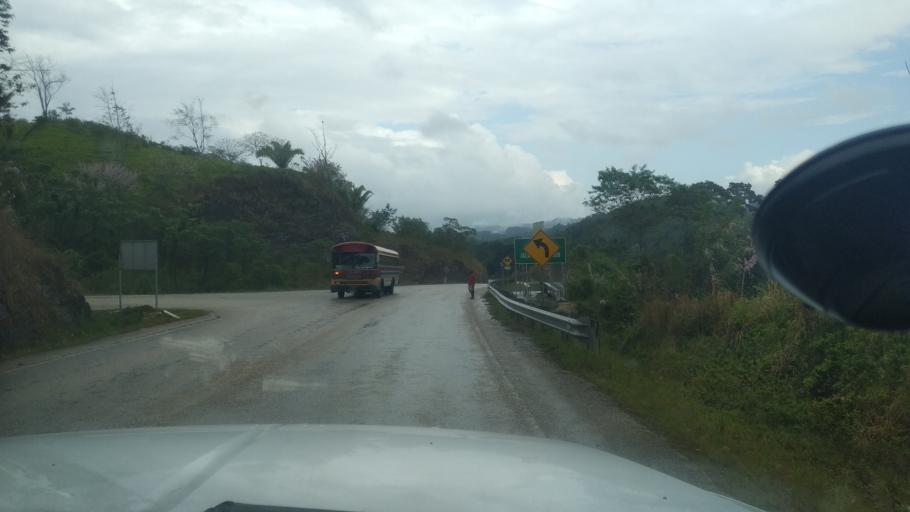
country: GT
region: Peten
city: San Luis
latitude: 16.1863
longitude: -89.1932
